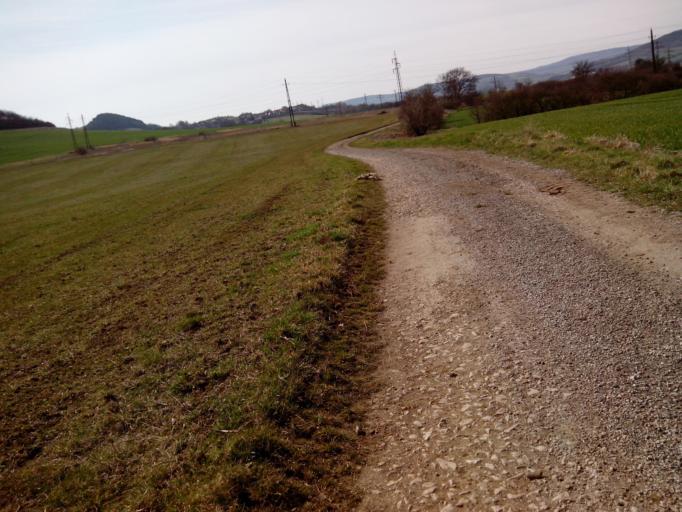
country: CZ
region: Central Bohemia
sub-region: Okres Beroun
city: Beroun
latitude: 49.9522
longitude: 14.0824
